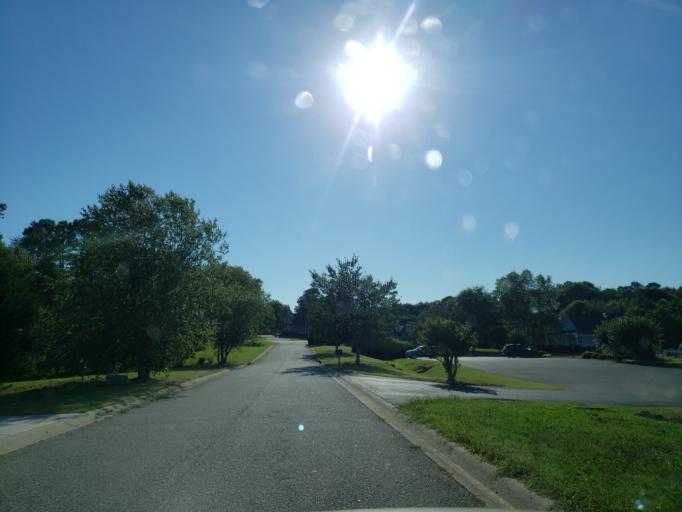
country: US
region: Georgia
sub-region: Bartow County
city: Euharlee
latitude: 34.1076
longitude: -84.9937
